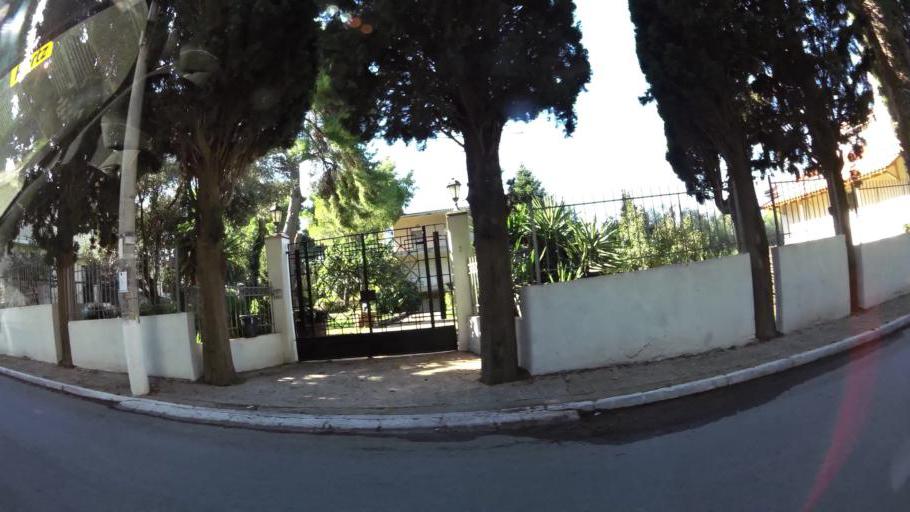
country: GR
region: Attica
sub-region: Nomarchia Anatolikis Attikis
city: Anoixi
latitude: 38.1312
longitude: 23.8620
